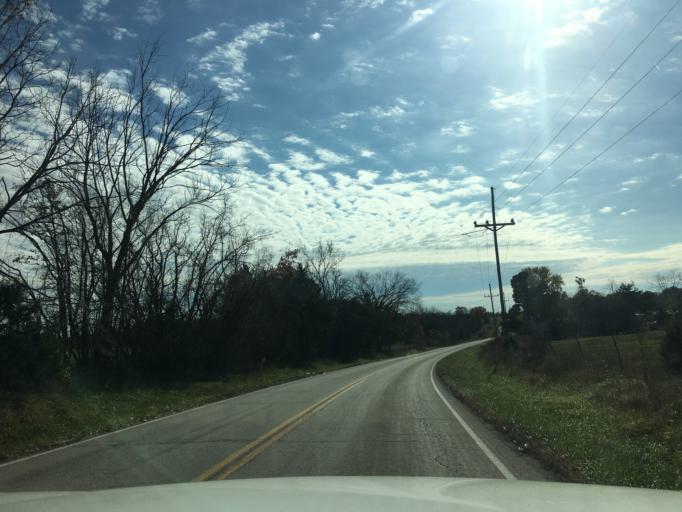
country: US
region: Missouri
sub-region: Osage County
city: Linn
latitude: 38.4072
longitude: -91.8174
